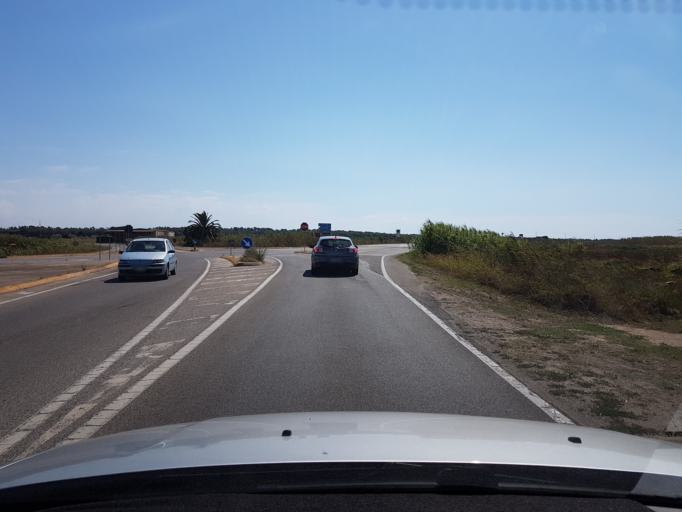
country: IT
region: Sardinia
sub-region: Provincia di Oristano
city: Cabras
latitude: 39.9194
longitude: 8.5210
